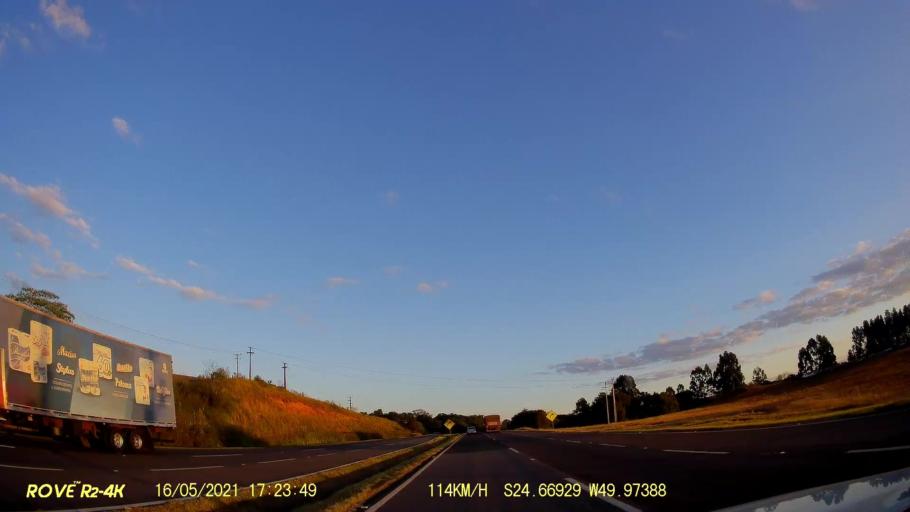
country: BR
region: Parana
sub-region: Castro
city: Castro
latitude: -24.6696
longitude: -49.9739
